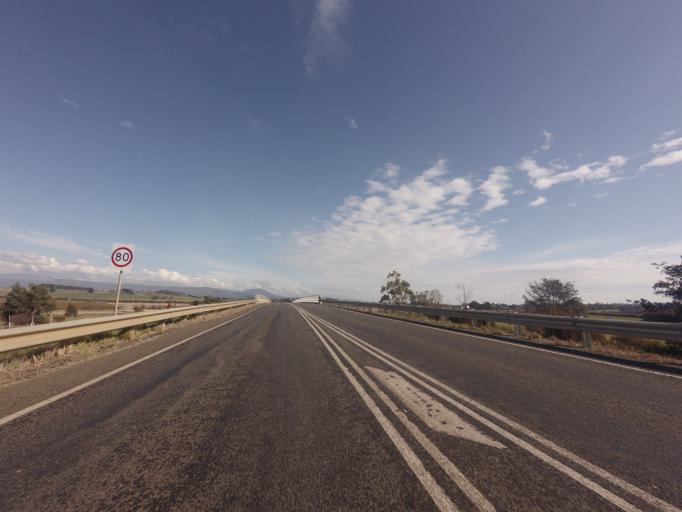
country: AU
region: Tasmania
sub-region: Meander Valley
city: Westbury
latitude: -41.5269
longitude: 146.8742
